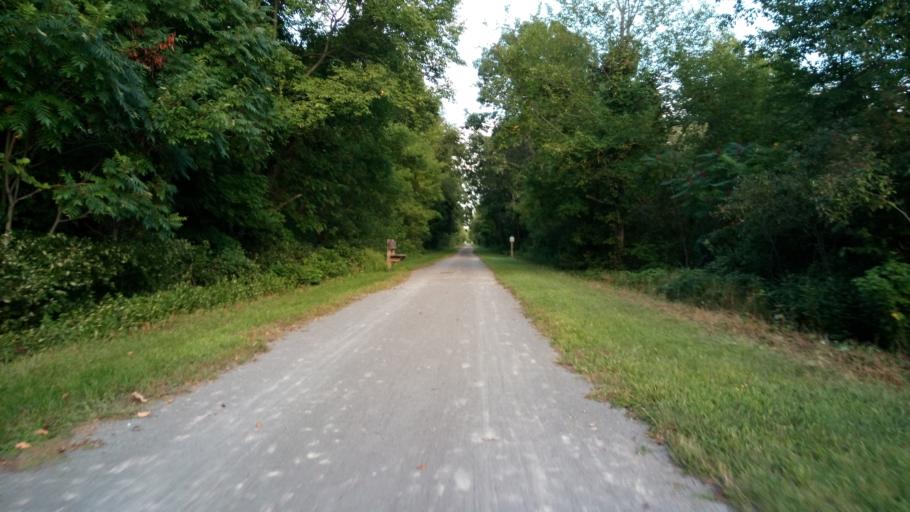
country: US
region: New York
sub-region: Ontario County
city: Victor
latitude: 43.0013
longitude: -77.4622
